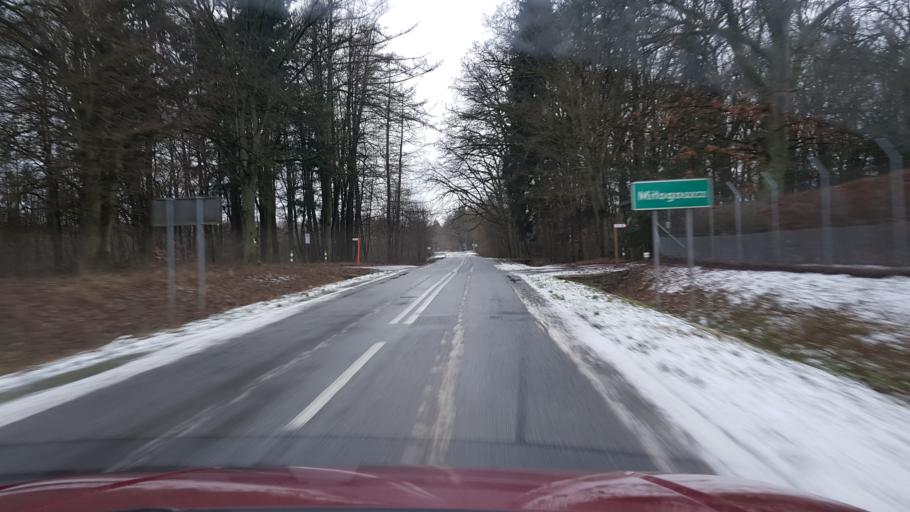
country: PL
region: West Pomeranian Voivodeship
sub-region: Powiat gryficki
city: Ploty
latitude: 53.7210
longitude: 15.3078
